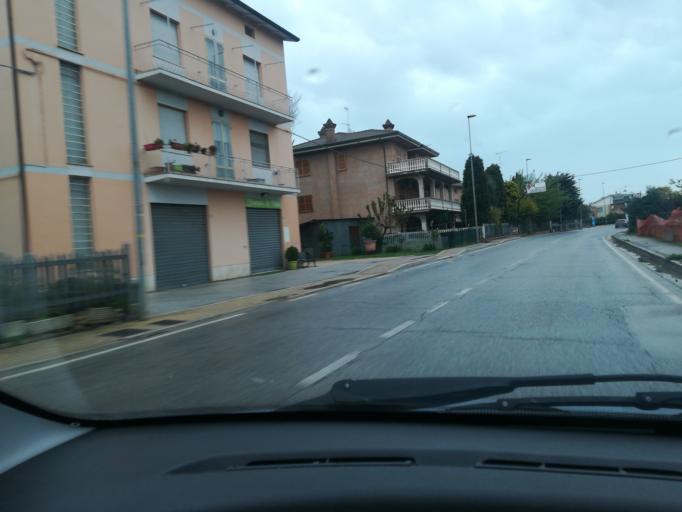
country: IT
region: The Marches
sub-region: Provincia di Macerata
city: Borgo Stazione
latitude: 43.2831
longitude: 13.6357
